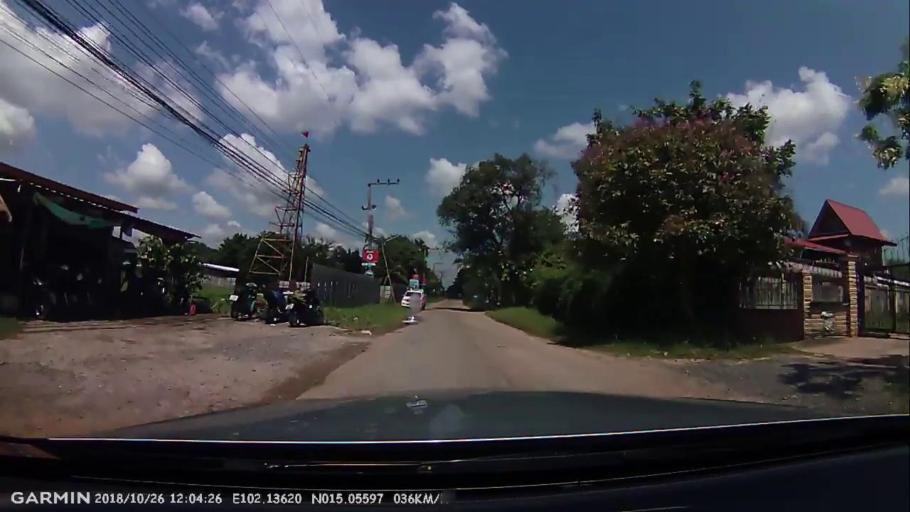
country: TH
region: Nakhon Ratchasima
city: Nakhon Ratchasima
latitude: 15.0560
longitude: 102.1362
